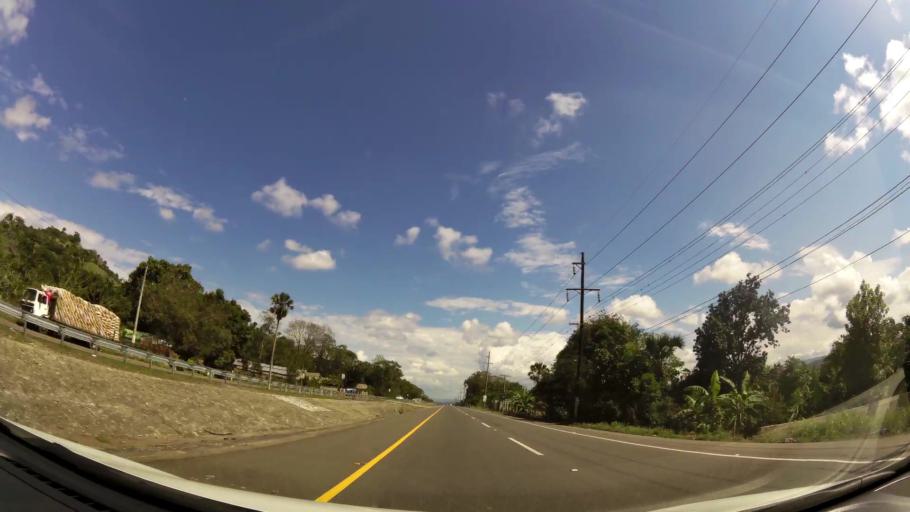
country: DO
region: La Vega
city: Concepcion de La Vega
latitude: 19.2572
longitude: -70.5678
